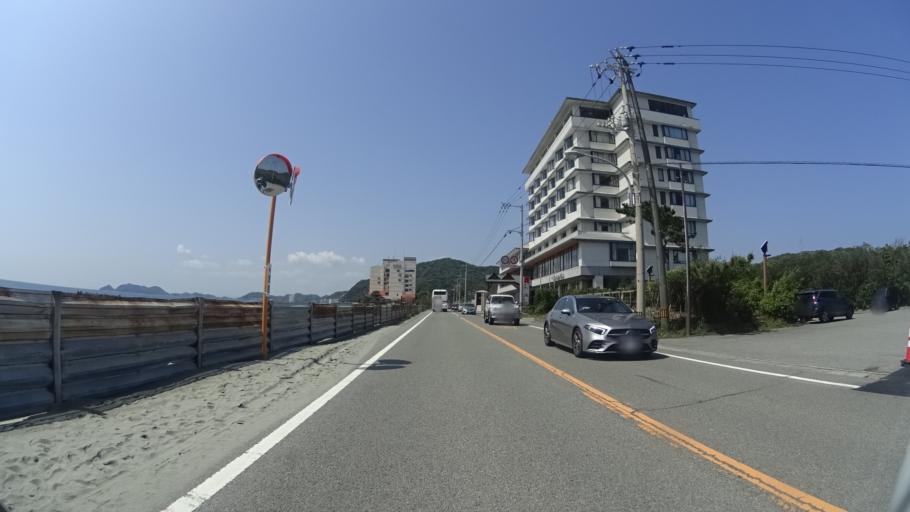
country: JP
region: Tokushima
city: Narutocho-mitsuishi
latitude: 34.2230
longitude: 134.6354
